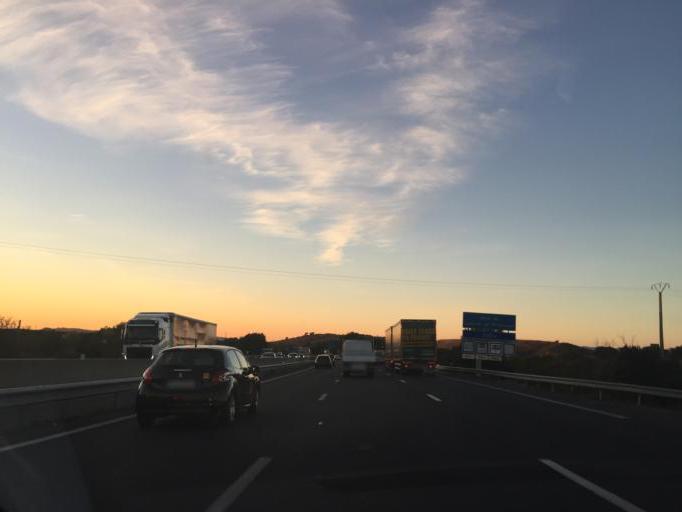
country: FR
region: Provence-Alpes-Cote d'Azur
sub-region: Departement des Bouches-du-Rhone
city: La Fare-les-Oliviers
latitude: 43.5870
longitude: 5.2004
